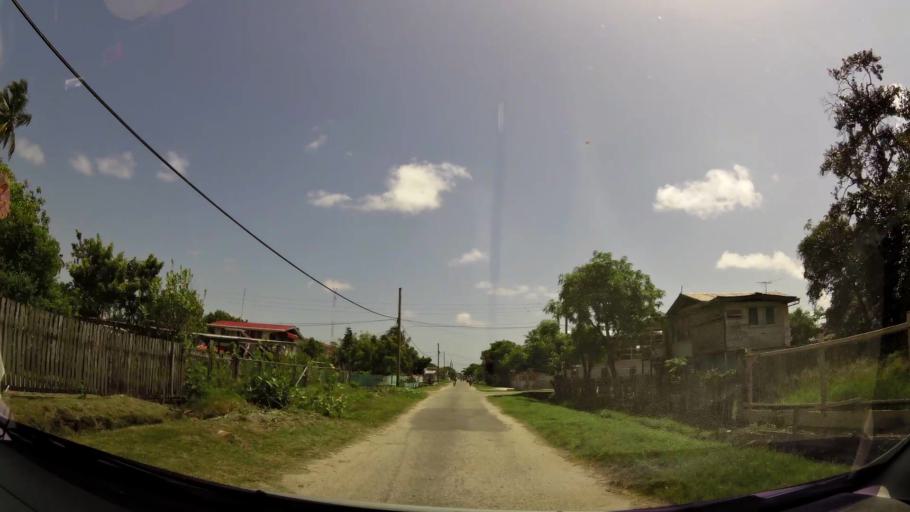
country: GY
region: Demerara-Mahaica
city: Mahaica Village
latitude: 6.7641
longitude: -58.0088
